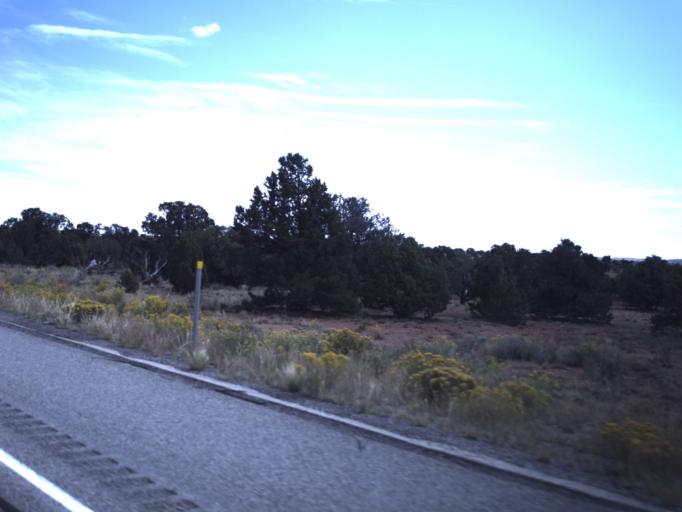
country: US
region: Utah
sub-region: Emery County
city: Castle Dale
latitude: 38.8675
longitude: -110.7162
